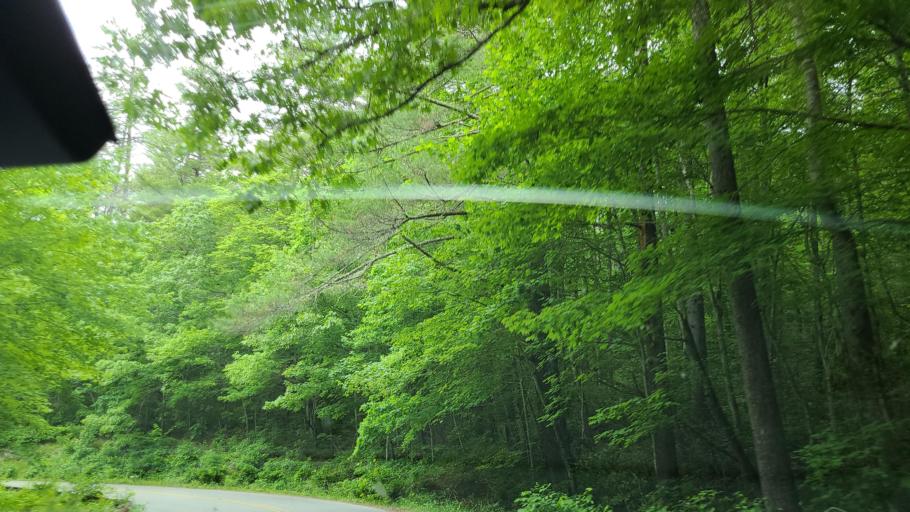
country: US
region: North Carolina
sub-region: Macon County
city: Franklin
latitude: 35.0828
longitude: -83.2599
